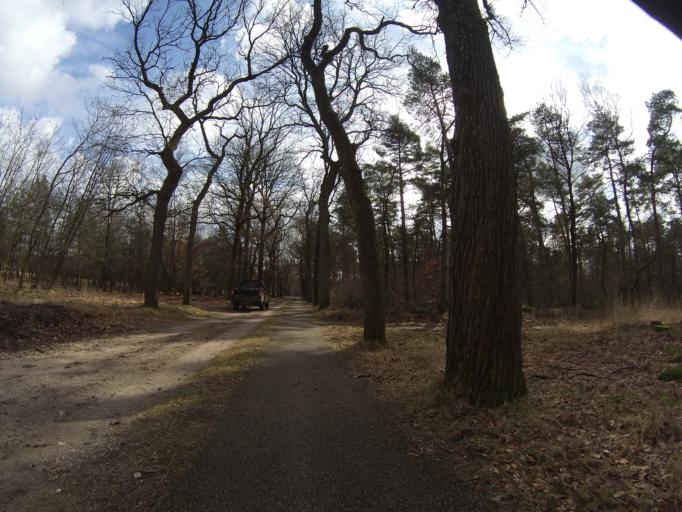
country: NL
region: Utrecht
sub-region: Gemeente Utrechtse Heuvelrug
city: Driebergen-Rijsenburg
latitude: 52.0983
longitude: 5.2984
